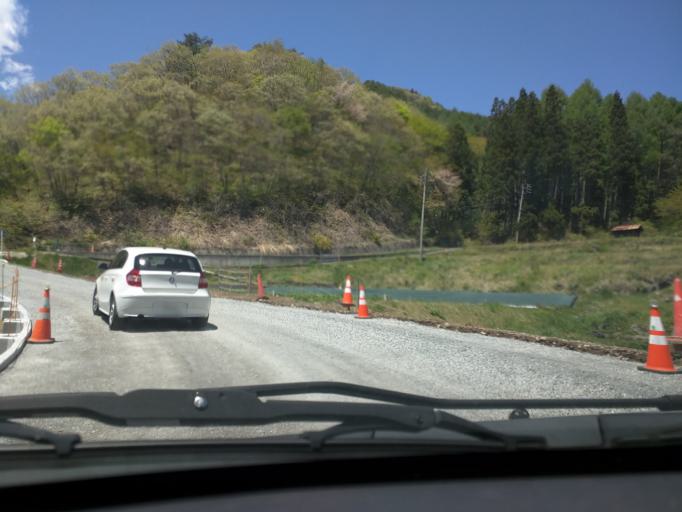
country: JP
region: Nagano
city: Nagano-shi
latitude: 36.6869
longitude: 138.1150
